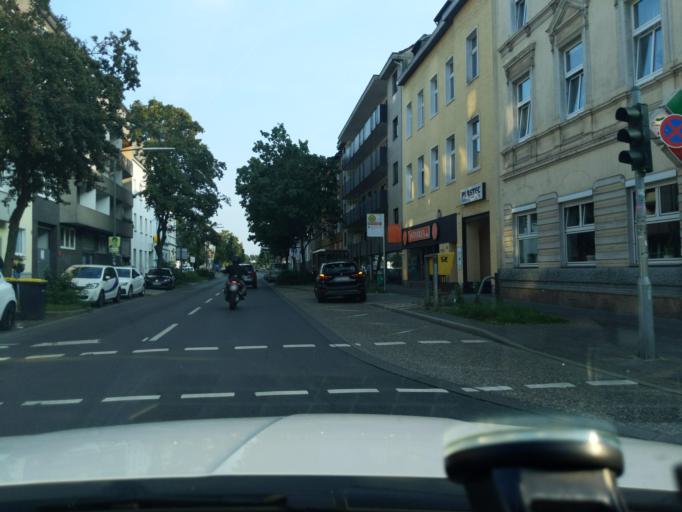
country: DE
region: North Rhine-Westphalia
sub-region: Regierungsbezirk Dusseldorf
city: Dusseldorf
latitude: 51.2117
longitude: 6.8097
